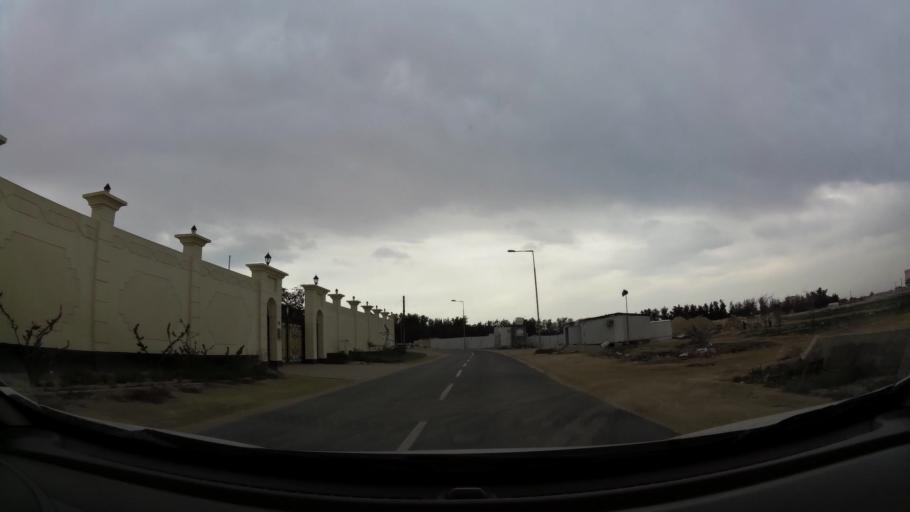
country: BH
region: Central Governorate
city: Madinat Hamad
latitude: 26.1452
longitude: 50.4732
